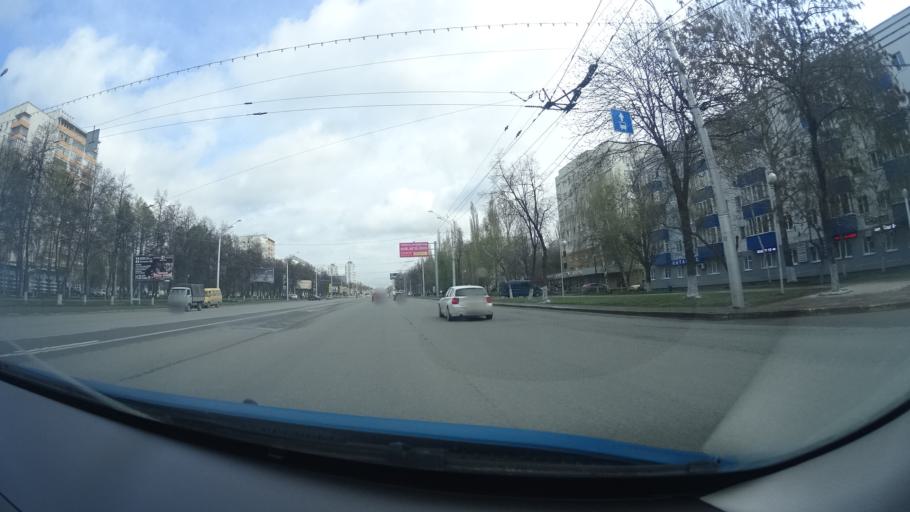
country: RU
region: Bashkortostan
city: Ufa
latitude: 54.7560
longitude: 56.0044
